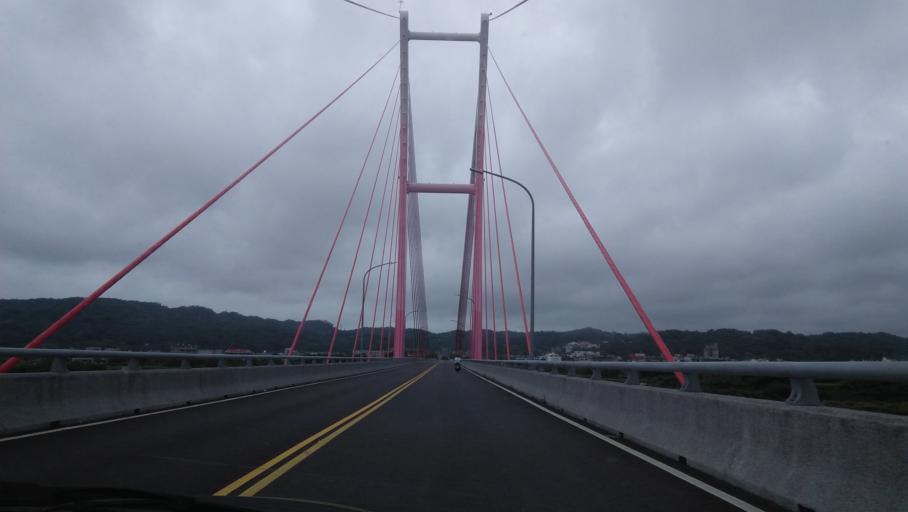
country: TW
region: Taiwan
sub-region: Hsinchu
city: Zhubei
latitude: 24.7853
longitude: 121.0562
